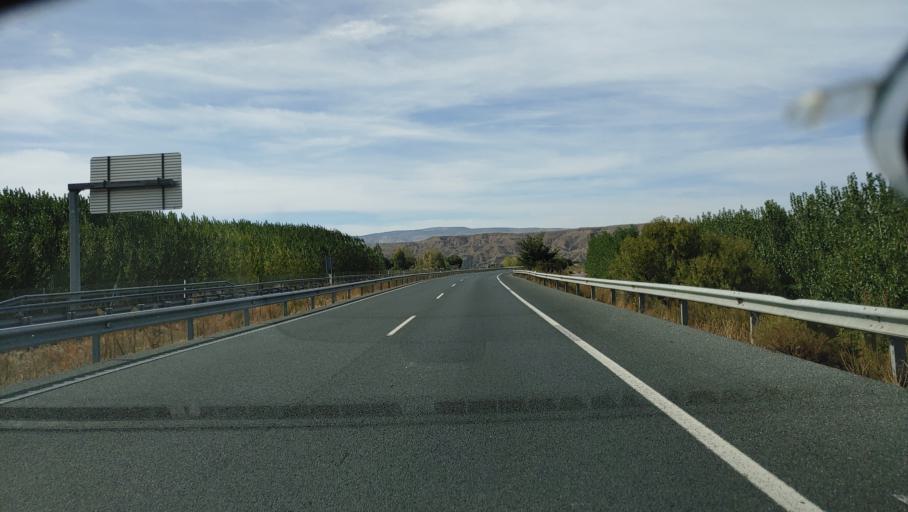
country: ES
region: Andalusia
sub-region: Provincia de Granada
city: Purullena
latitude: 37.3249
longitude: -3.1727
